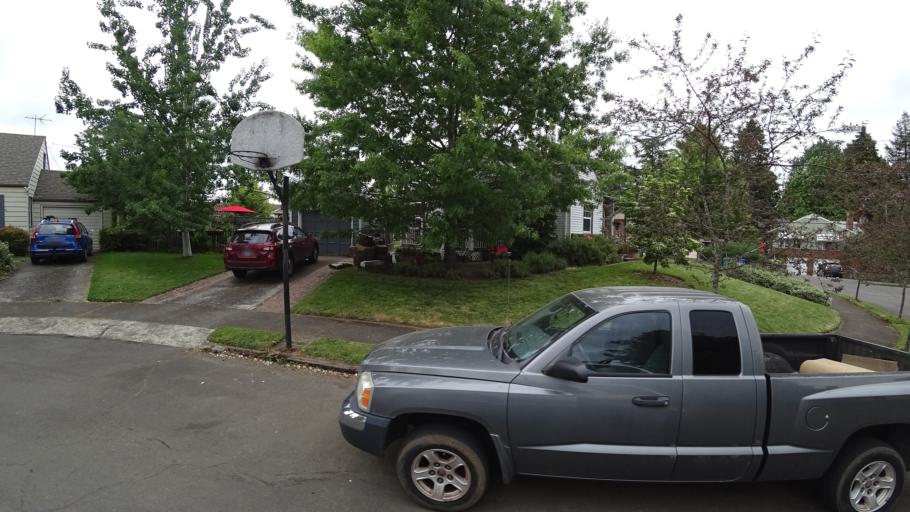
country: US
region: Oregon
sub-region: Multnomah County
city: Lents
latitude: 45.5210
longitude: -122.6107
